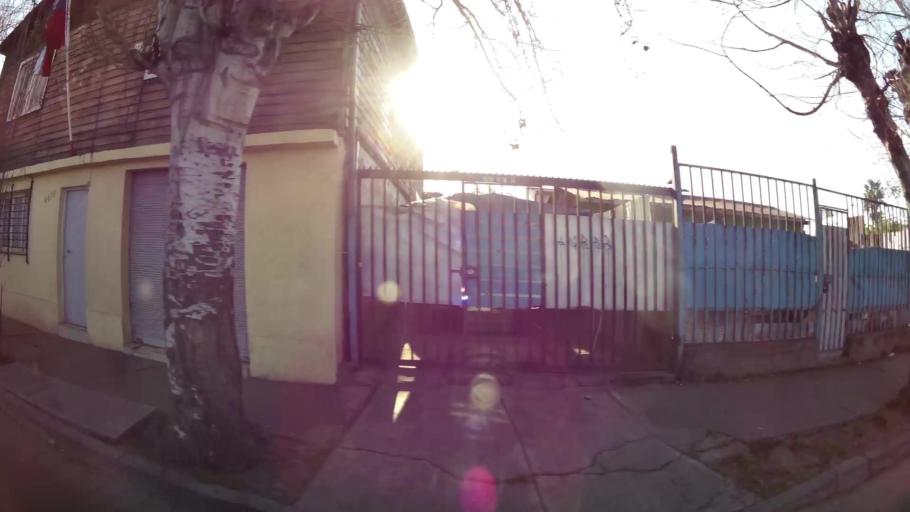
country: CL
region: Santiago Metropolitan
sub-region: Provincia de Santiago
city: Santiago
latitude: -33.3861
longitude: -70.6715
